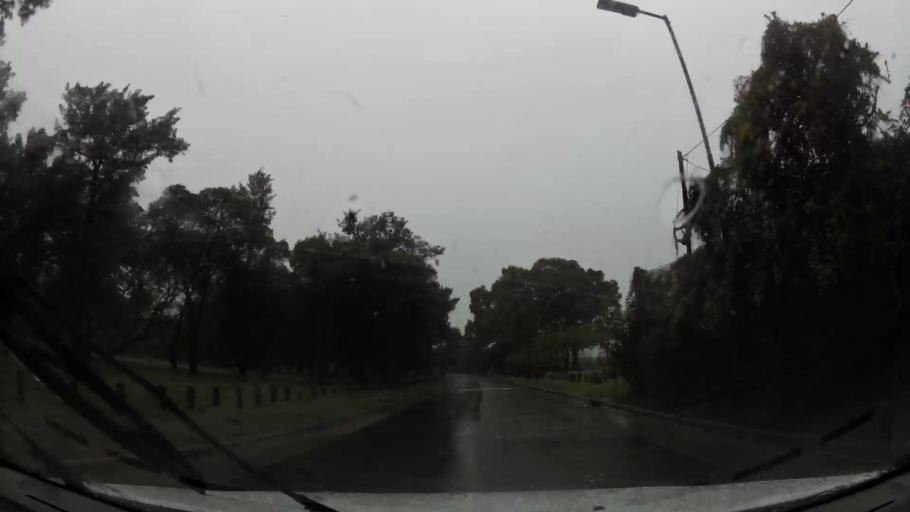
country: AR
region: Buenos Aires F.D.
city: Colegiales
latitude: -34.5621
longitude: -58.4293
